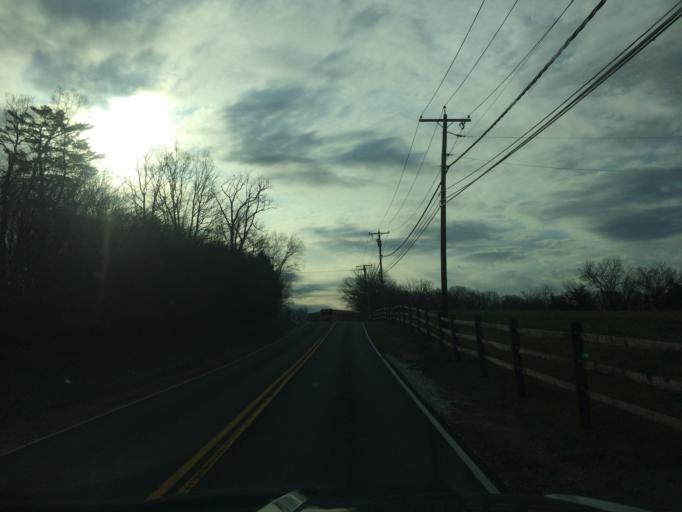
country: US
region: Maryland
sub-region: Howard County
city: North Laurel
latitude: 39.1509
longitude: -76.8621
